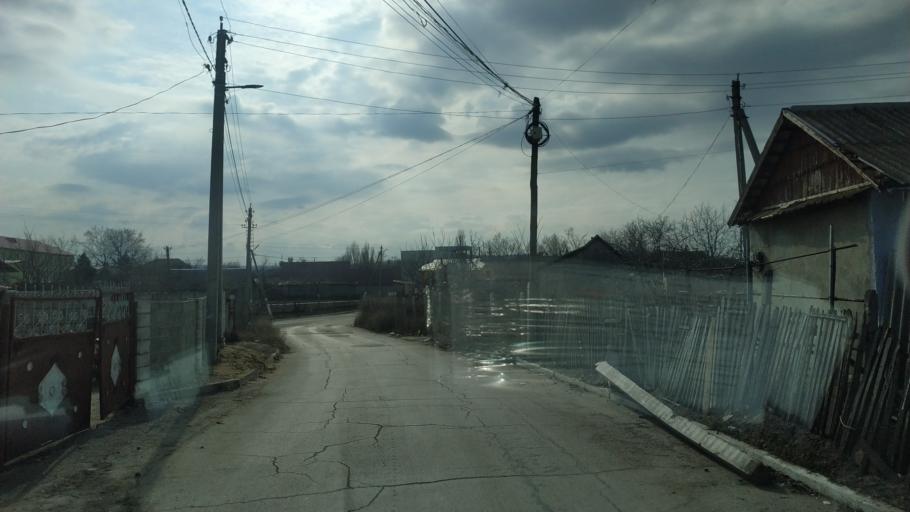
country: MD
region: Anenii Noi
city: Anenii Noi
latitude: 46.9030
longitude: 29.1398
